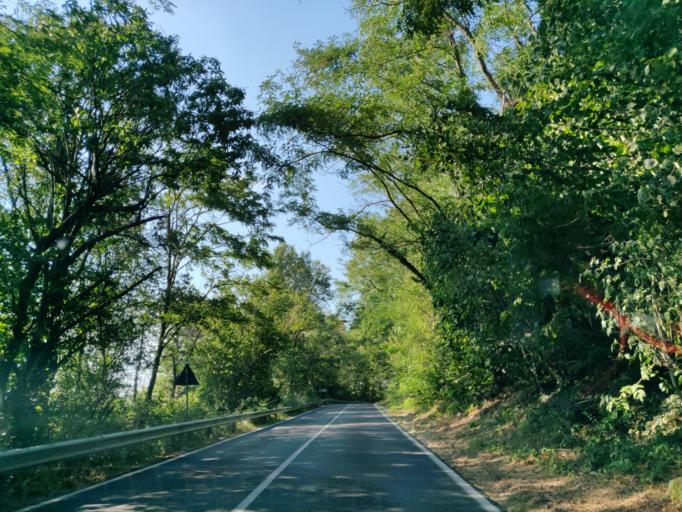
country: IT
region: Latium
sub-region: Provincia di Viterbo
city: Latera
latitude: 42.6225
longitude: 11.8380
